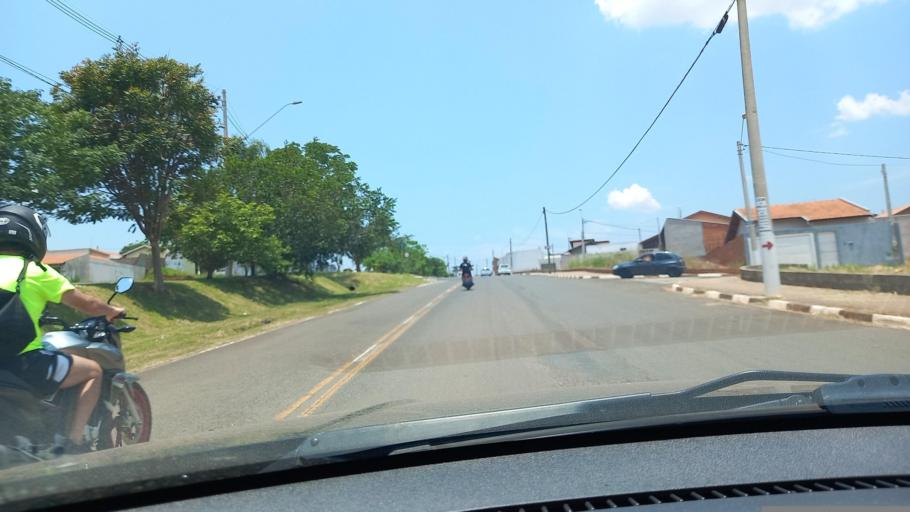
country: BR
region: Sao Paulo
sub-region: Itapira
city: Itapira
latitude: -22.4082
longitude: -46.8429
